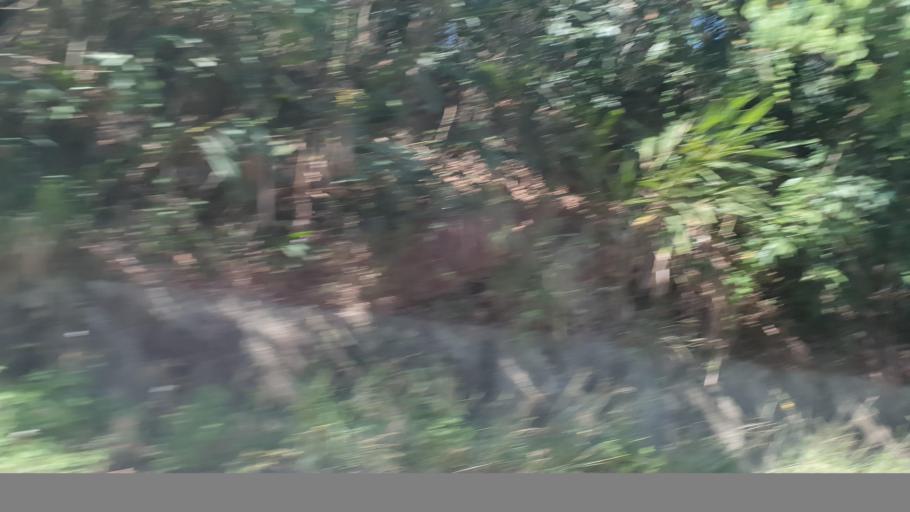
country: TW
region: Taiwan
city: Yujing
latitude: 23.0545
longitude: 120.3787
